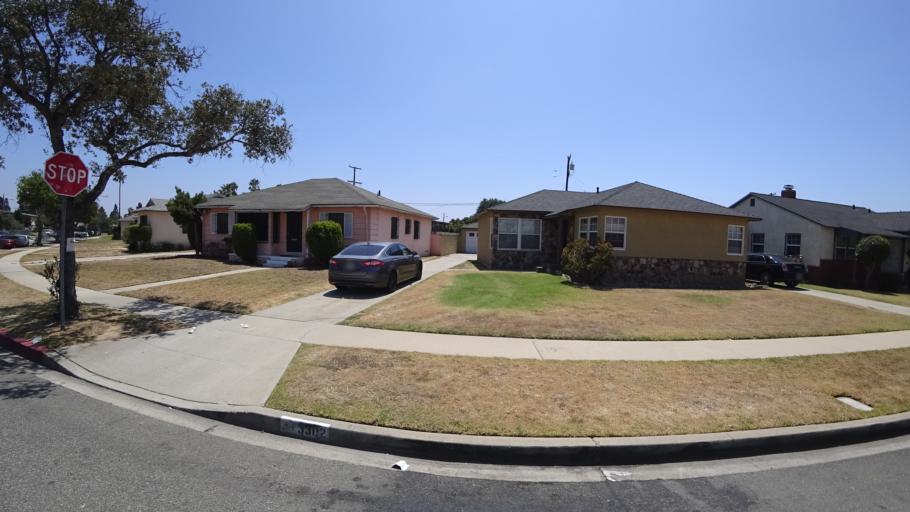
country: US
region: California
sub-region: Los Angeles County
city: Lennox
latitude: 33.9300
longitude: -118.3292
